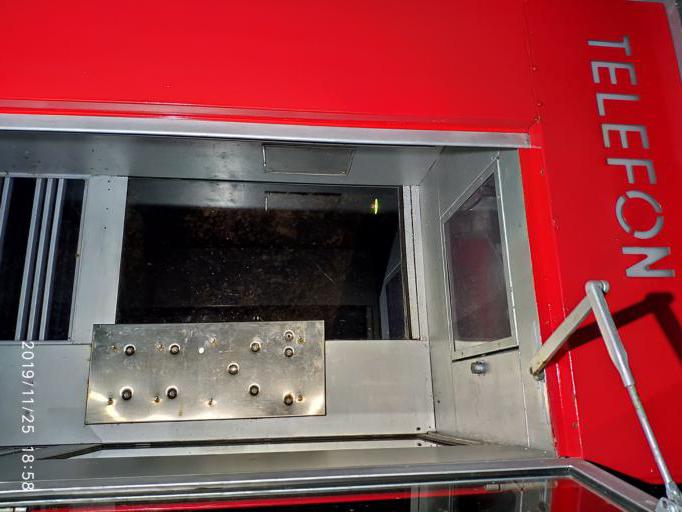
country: NO
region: Rogaland
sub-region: Suldal
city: Sand
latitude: 59.4835
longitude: 6.2525
